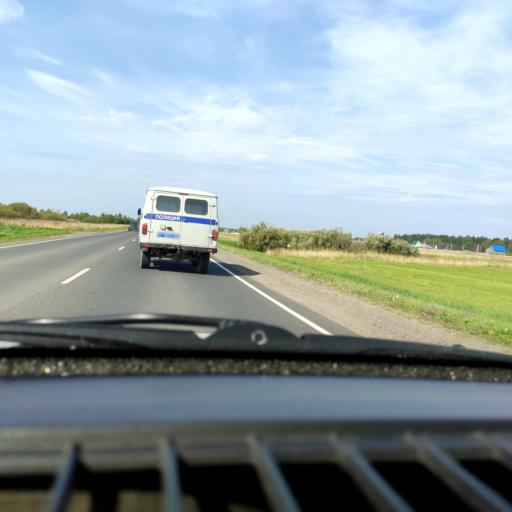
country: RU
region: Perm
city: Ust'-Kachka
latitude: 57.9782
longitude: 55.7223
